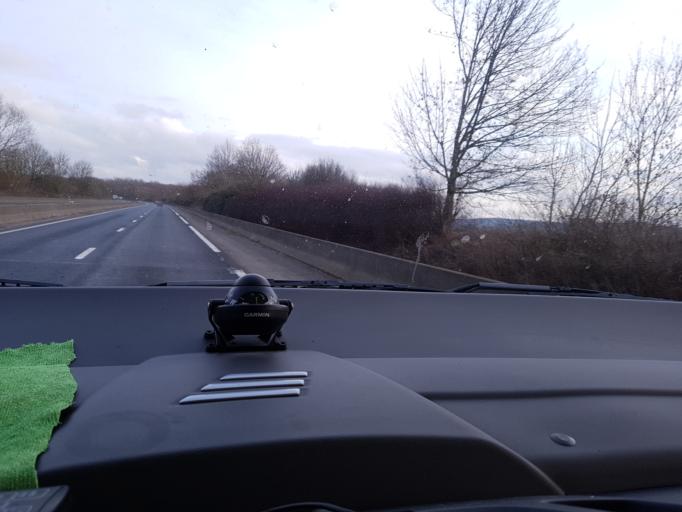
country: FR
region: Champagne-Ardenne
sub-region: Departement des Ardennes
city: Balan
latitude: 49.6844
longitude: 4.9573
